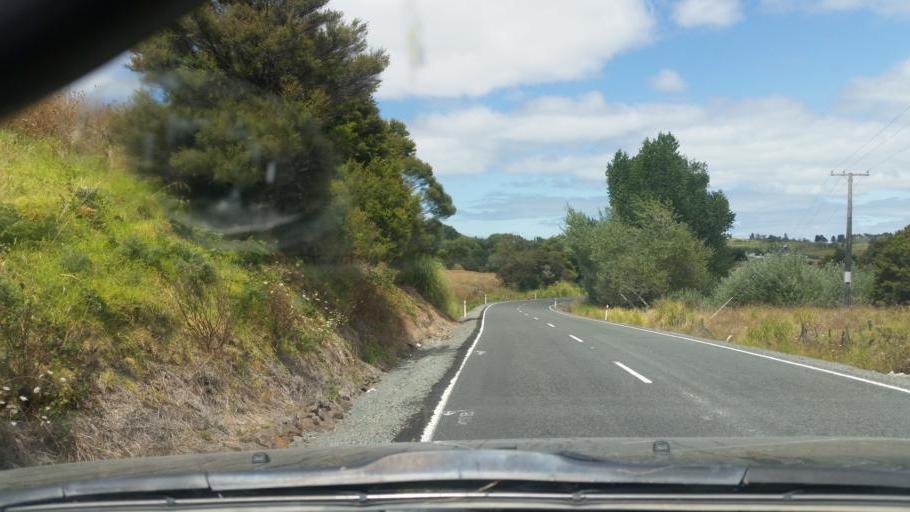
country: NZ
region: Auckland
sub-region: Auckland
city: Wellsford
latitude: -36.1271
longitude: 174.3284
